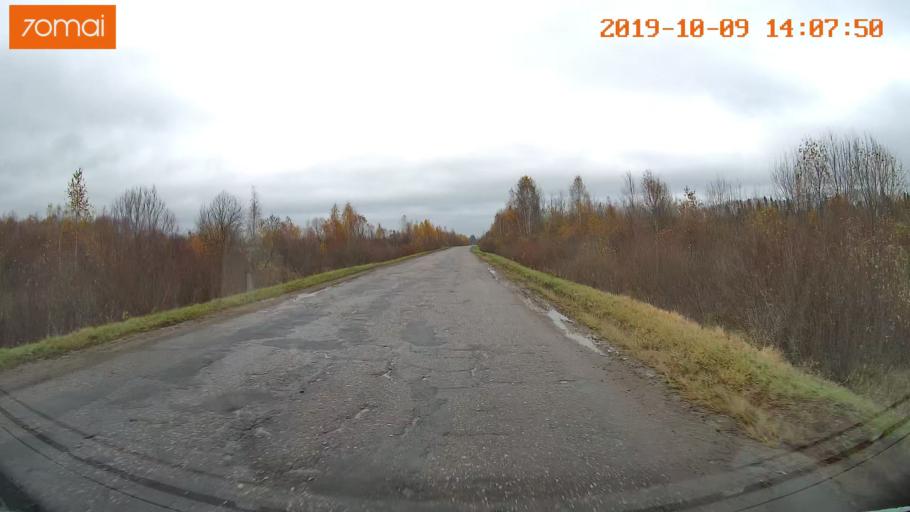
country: RU
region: Kostroma
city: Buy
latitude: 58.4731
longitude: 41.4280
